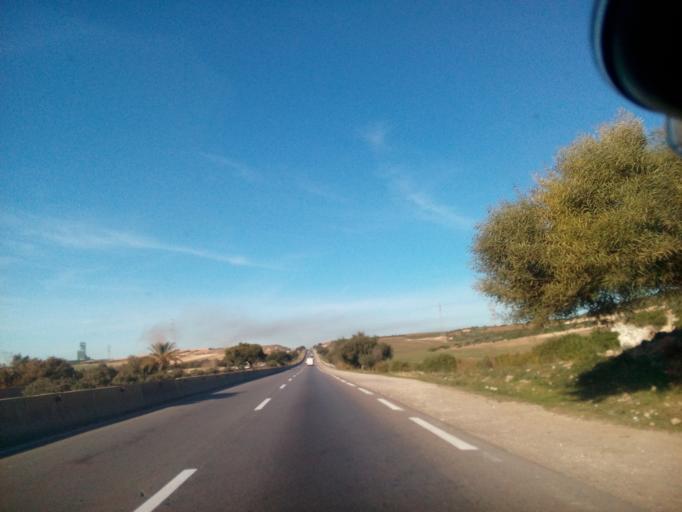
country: DZ
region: Oran
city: Ain el Bya
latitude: 35.7692
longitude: -0.2353
